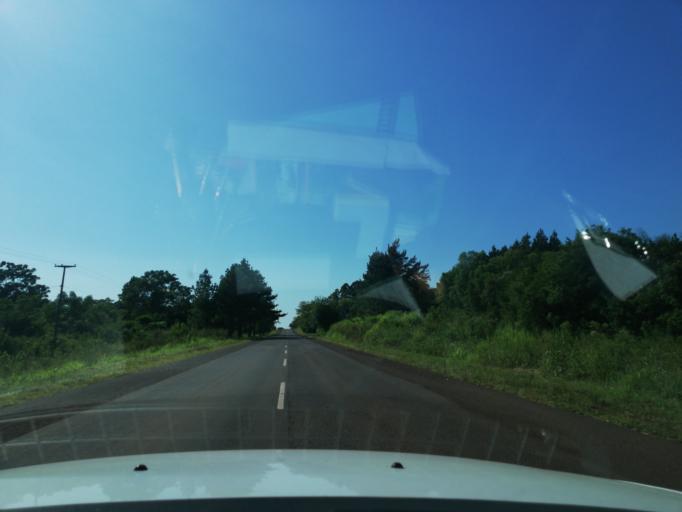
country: AR
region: Misiones
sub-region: Departamento de Leandro N. Alem
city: Leandro N. Alem
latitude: -27.5768
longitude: -55.3805
